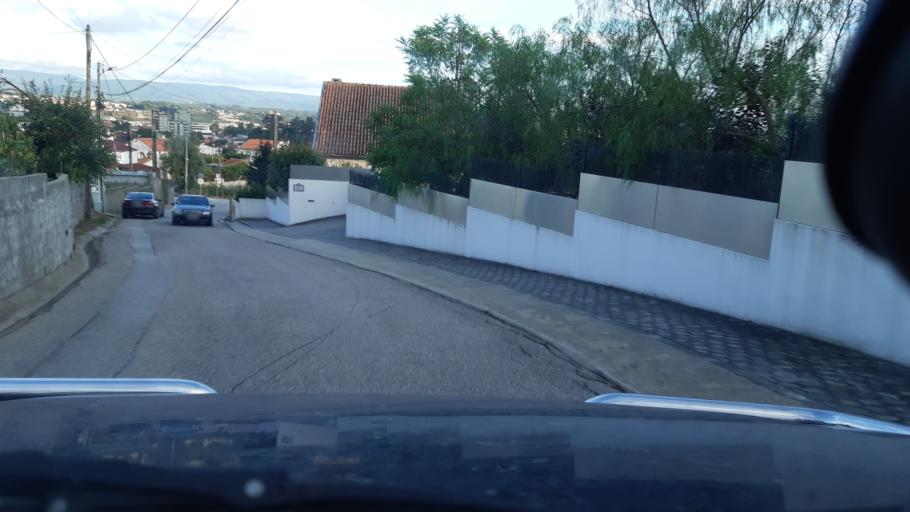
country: PT
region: Aveiro
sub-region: Agueda
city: Agueda
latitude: 40.5775
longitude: -8.4579
